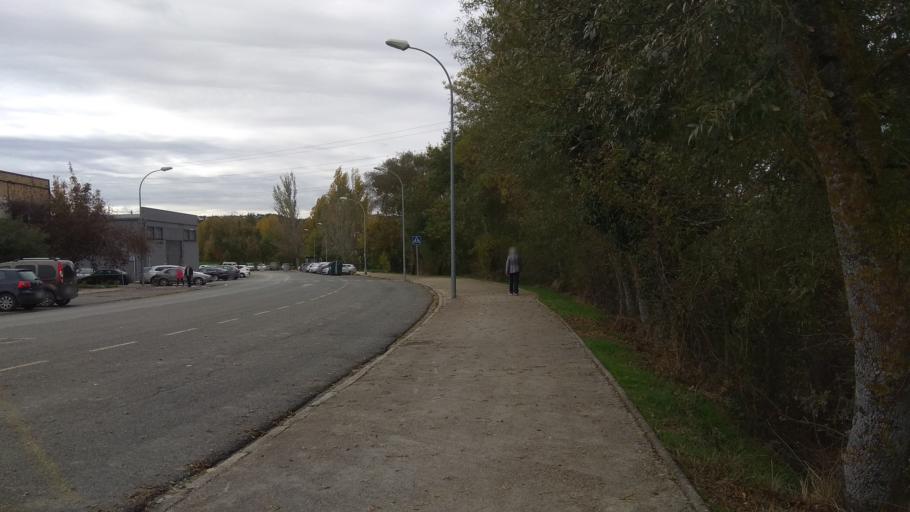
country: ES
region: Navarre
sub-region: Provincia de Navarra
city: Baranain
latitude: 42.8086
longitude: -1.6913
